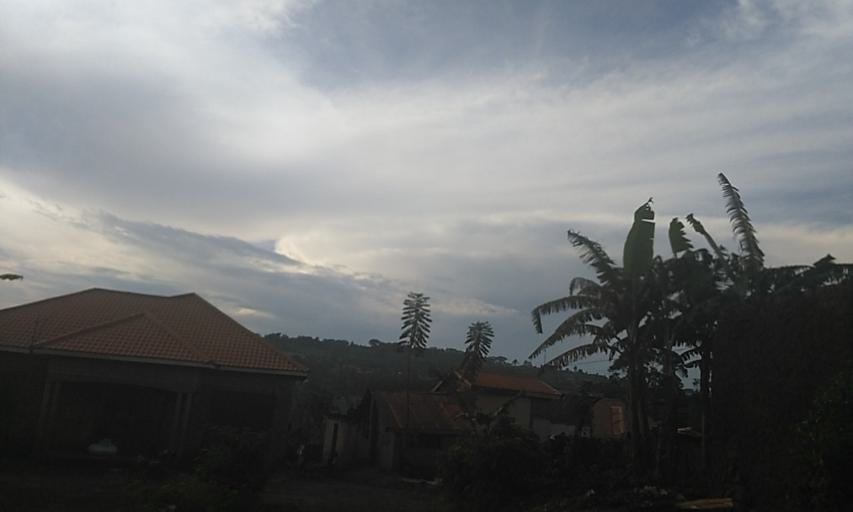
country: UG
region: Central Region
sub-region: Wakiso District
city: Kajansi
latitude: 0.2451
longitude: 32.4998
